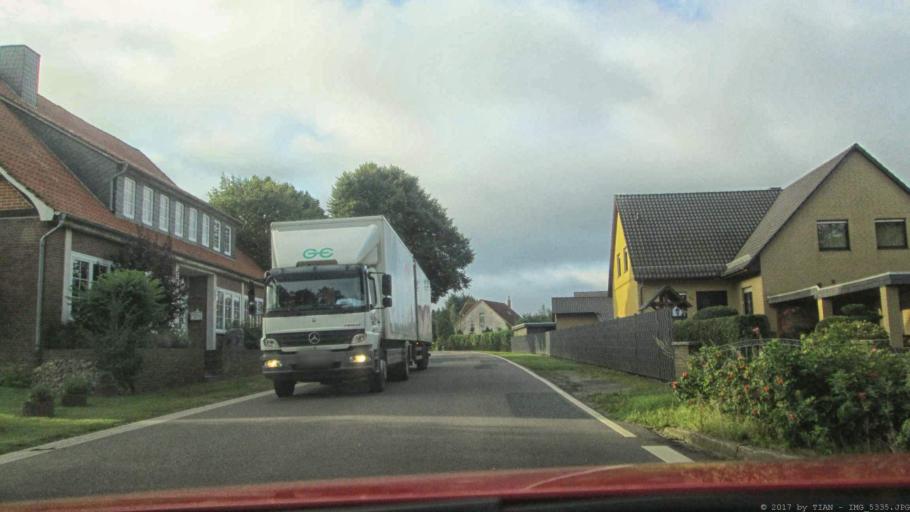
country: DE
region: Lower Saxony
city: Wittingen
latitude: 52.7602
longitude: 10.7094
